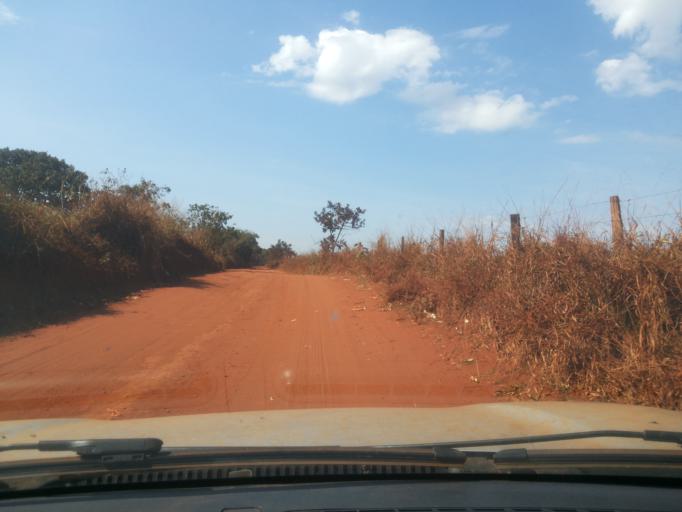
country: BR
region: Minas Gerais
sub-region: Ituiutaba
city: Ituiutaba
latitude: -19.0056
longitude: -49.4061
